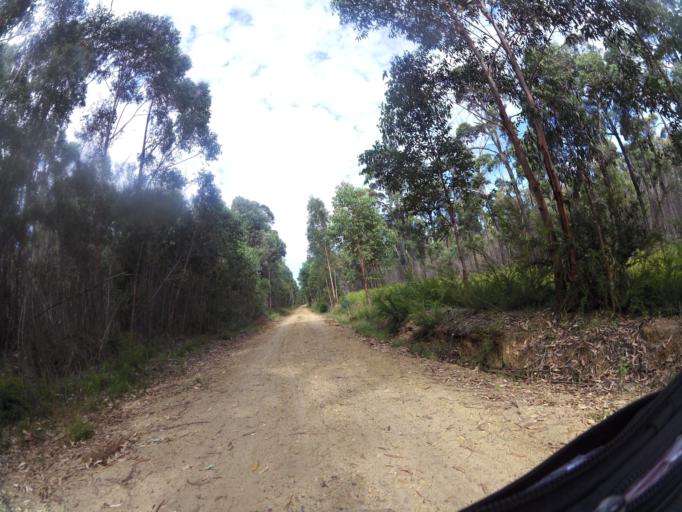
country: AU
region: Victoria
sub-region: East Gippsland
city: Lakes Entrance
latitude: -37.7454
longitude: 148.2478
